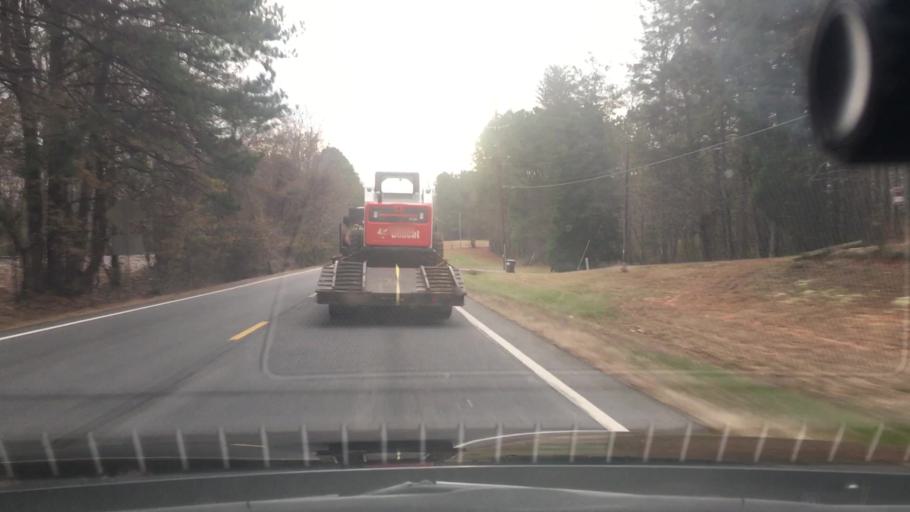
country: US
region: Georgia
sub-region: Coweta County
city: Senoia
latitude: 33.3172
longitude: -84.6173
